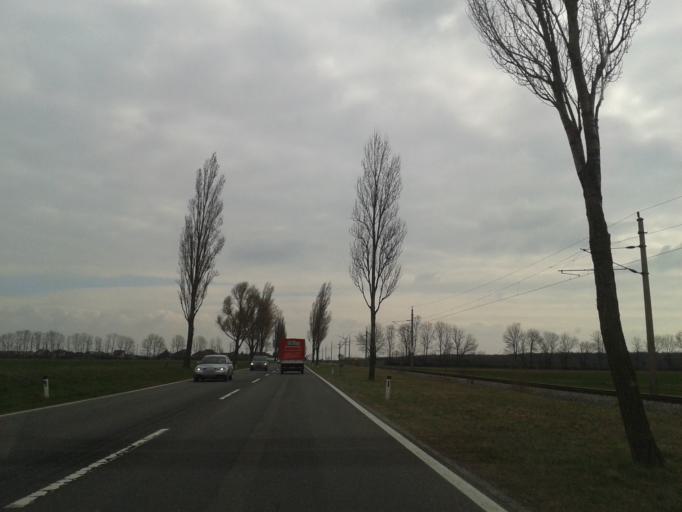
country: AT
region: Lower Austria
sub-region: Politischer Bezirk Ganserndorf
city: Orth an der Donau
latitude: 48.1104
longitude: 16.7003
